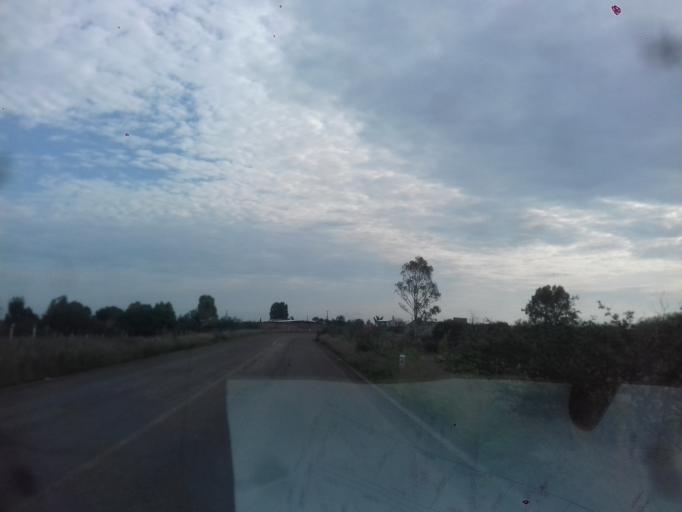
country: MX
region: Aguascalientes
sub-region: Aguascalientes
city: Villa Licenciado Jesus Teran (Calvillito)
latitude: 21.7919
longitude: -102.2256
